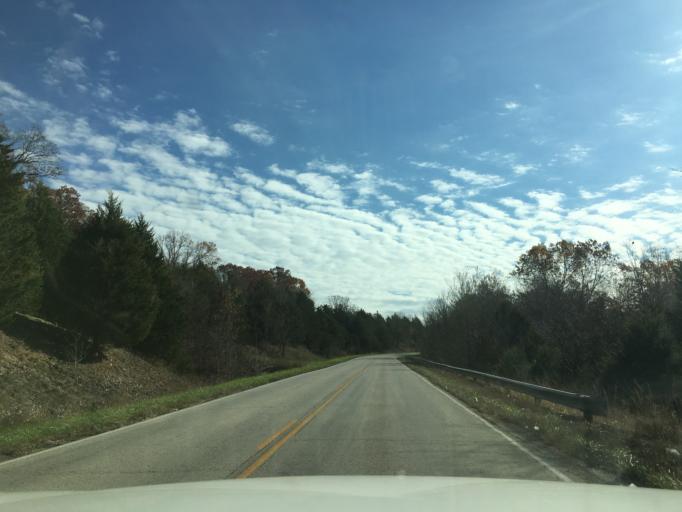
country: US
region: Missouri
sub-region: Osage County
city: Linn
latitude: 38.3848
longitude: -91.8137
